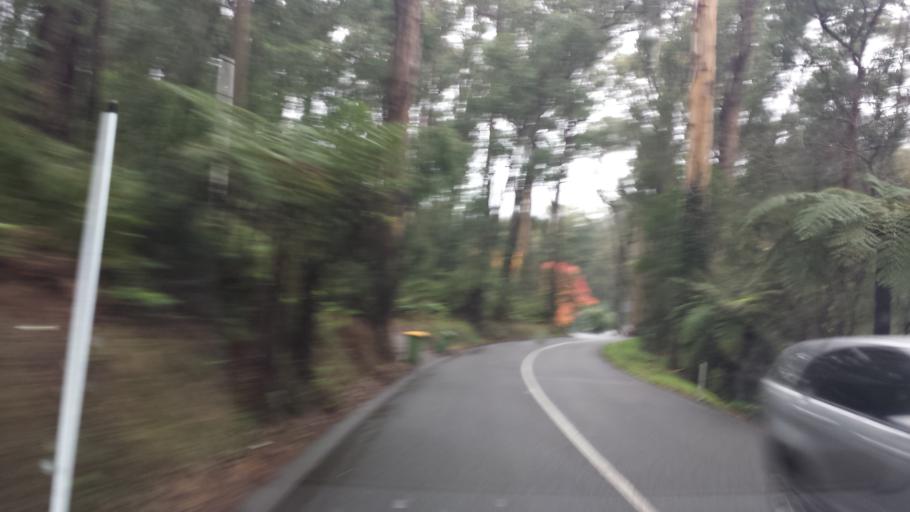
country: AU
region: Victoria
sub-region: Yarra Ranges
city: Monbulk
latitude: -37.8805
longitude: 145.4064
